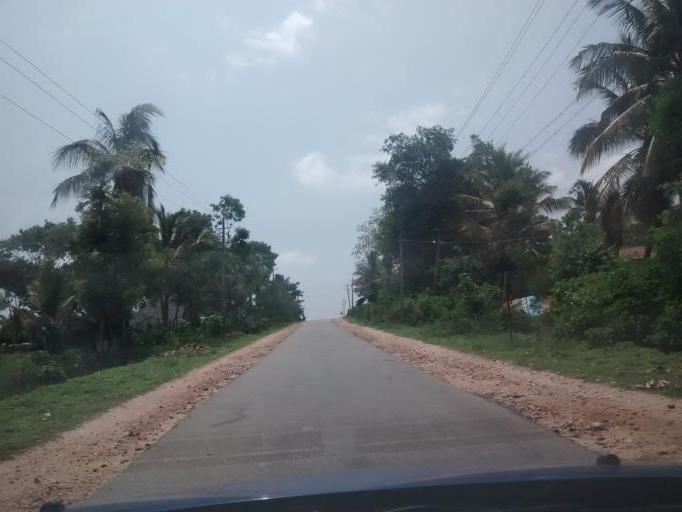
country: IN
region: Karnataka
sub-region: Mandya
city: Krishnarajpet
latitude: 12.5701
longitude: 76.2885
